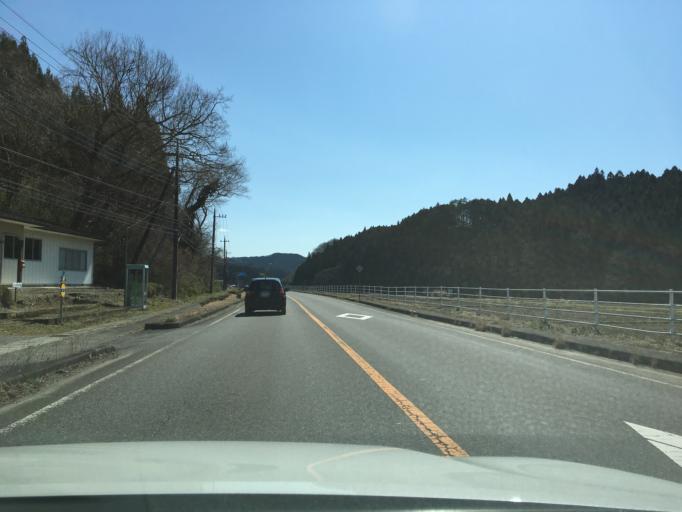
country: JP
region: Tochigi
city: Kuroiso
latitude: 37.0255
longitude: 140.1770
